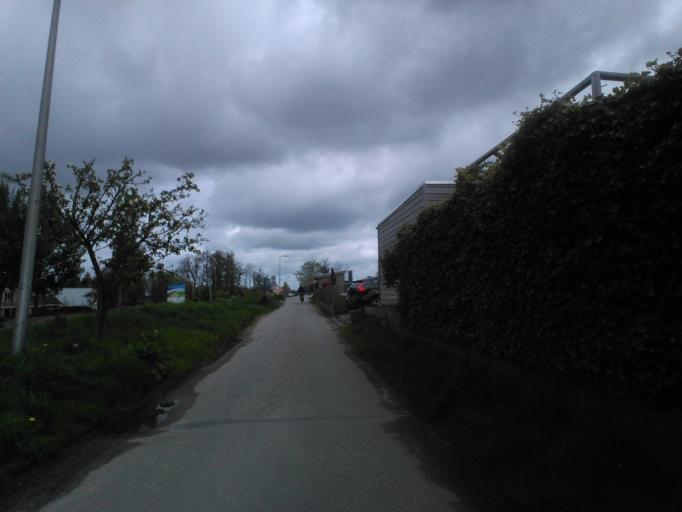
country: NL
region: South Holland
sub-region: Gemeente Gouda
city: Bloemendaal
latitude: 51.9919
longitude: 4.6729
